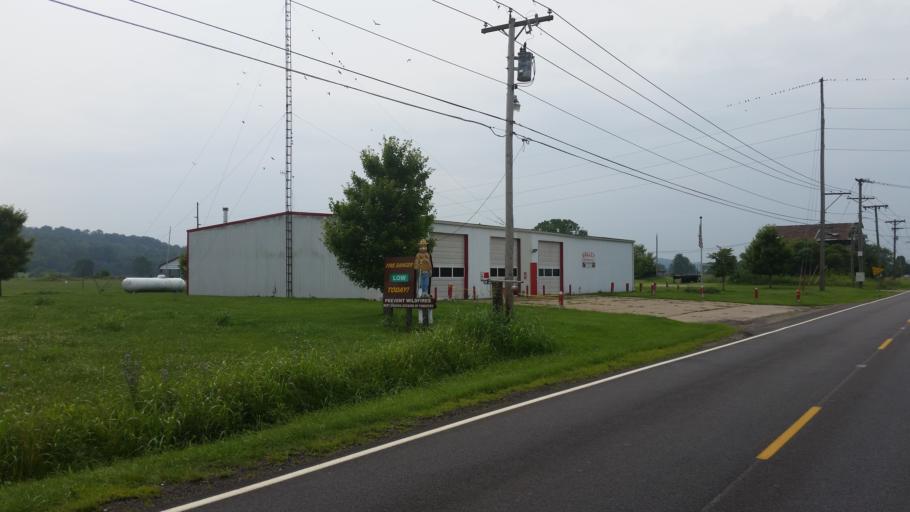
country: US
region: Ohio
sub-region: Gallia County
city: Gallipolis
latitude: 38.6605
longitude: -82.1682
